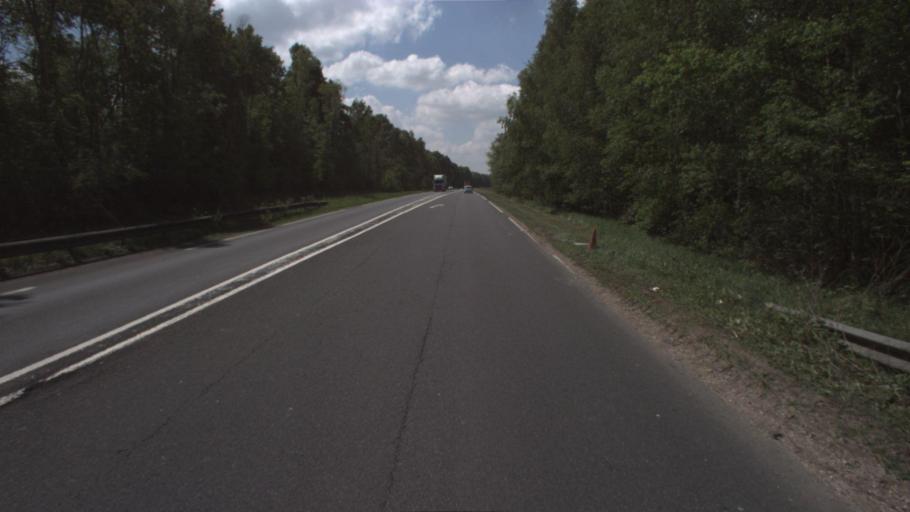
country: FR
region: Ile-de-France
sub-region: Departement de Seine-et-Marne
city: Guignes
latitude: 48.6534
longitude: 2.8052
